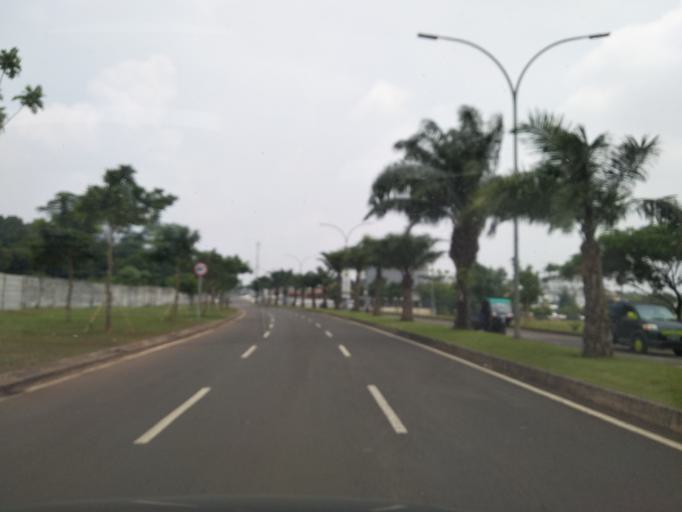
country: ID
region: West Java
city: Bekasi
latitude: -6.2943
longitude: 107.0458
